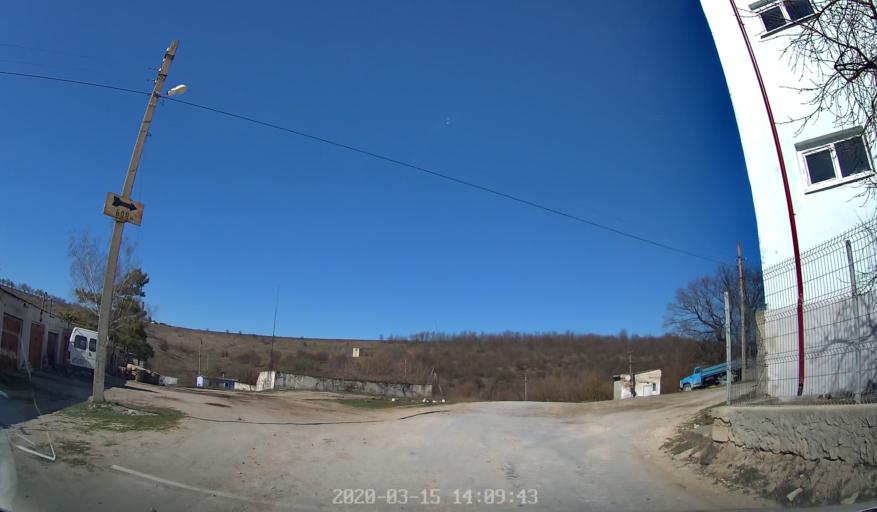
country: MD
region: Orhei
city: Orhei
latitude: 47.3115
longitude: 28.9321
